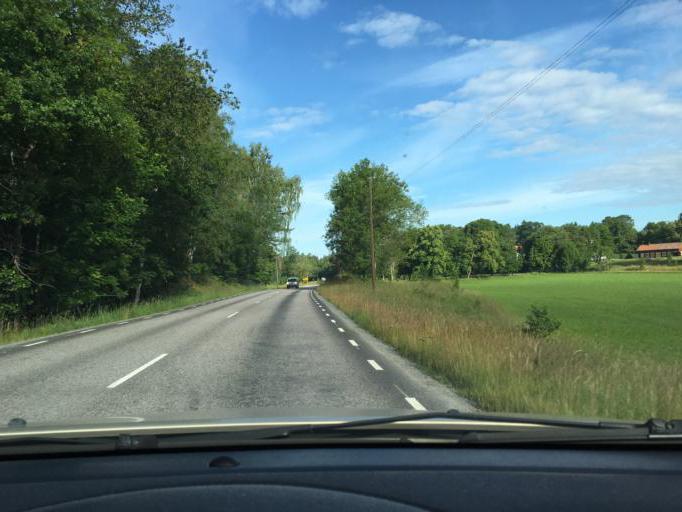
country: SE
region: Stockholm
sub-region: Salems Kommun
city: Ronninge
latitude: 59.2307
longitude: 17.7133
